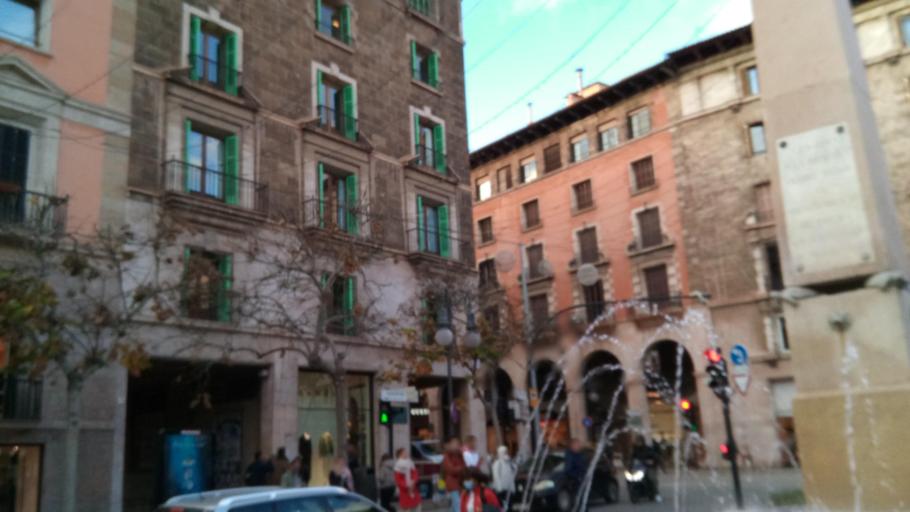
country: ES
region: Balearic Islands
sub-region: Illes Balears
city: Palma
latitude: 39.5711
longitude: 2.6463
